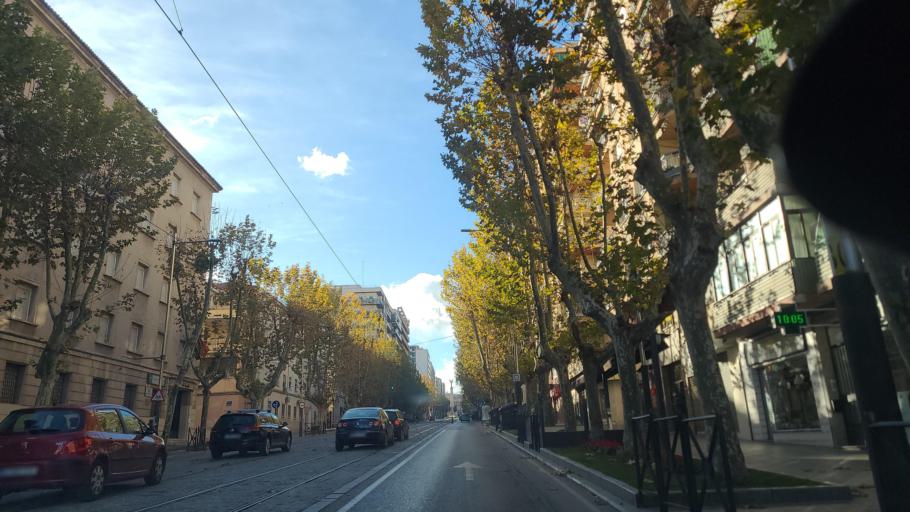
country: ES
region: Andalusia
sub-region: Provincia de Jaen
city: Jaen
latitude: 37.7756
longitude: -3.7893
